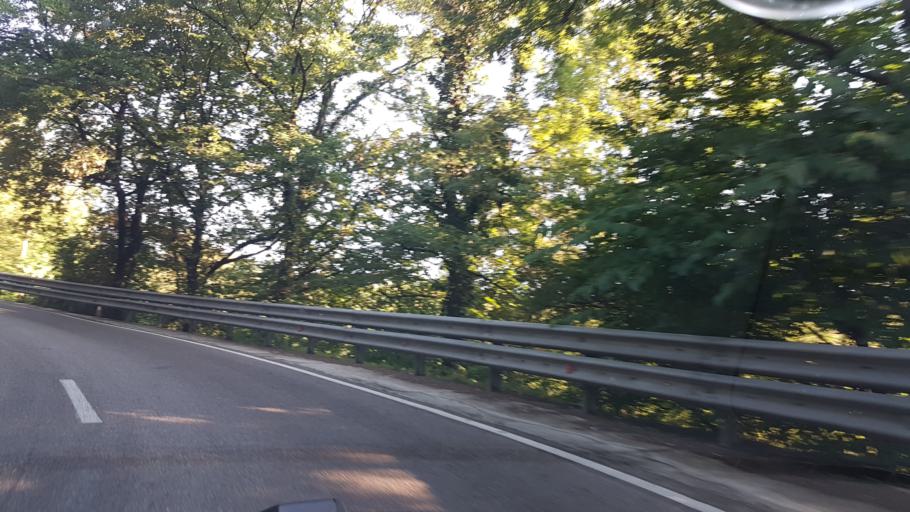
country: RU
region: Krasnodarskiy
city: Dagomys
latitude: 43.6457
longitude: 39.6966
